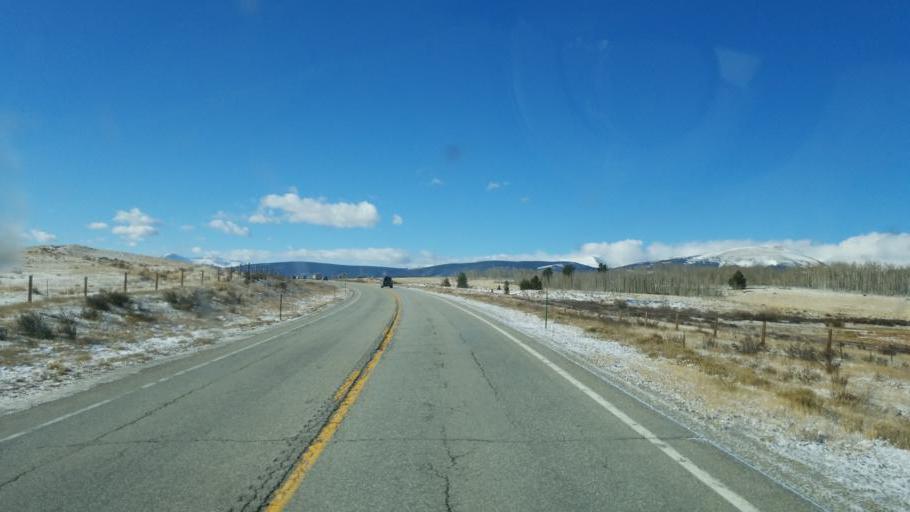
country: US
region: Colorado
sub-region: Park County
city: Fairplay
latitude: 39.2356
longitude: -105.9841
